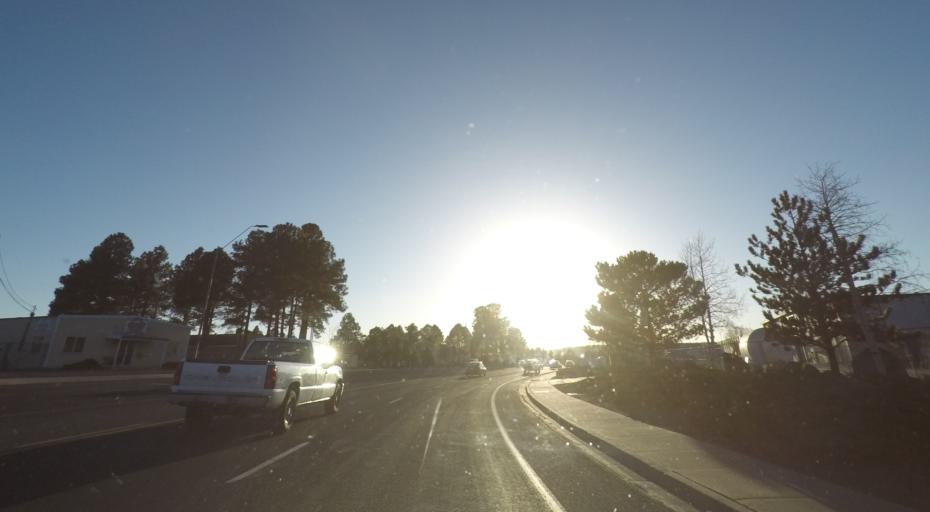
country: US
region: Arizona
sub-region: Coconino County
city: Flagstaff
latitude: 35.1912
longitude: -111.6319
